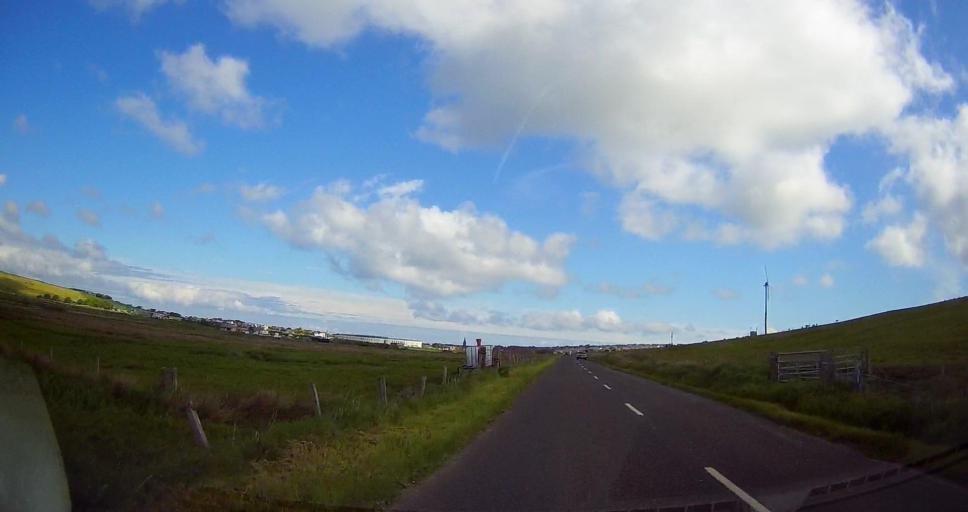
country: GB
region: Scotland
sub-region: Orkney Islands
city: Orkney
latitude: 58.9643
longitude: -2.9666
